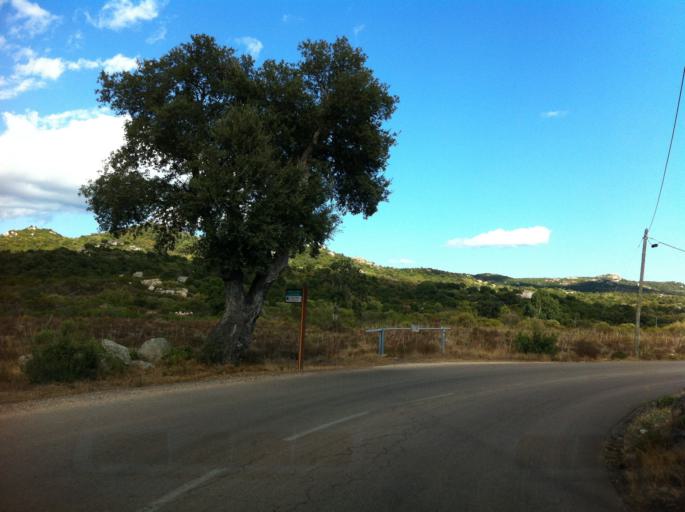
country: FR
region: Corsica
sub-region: Departement de la Corse-du-Sud
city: Porto-Vecchio
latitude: 41.6367
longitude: 9.2938
